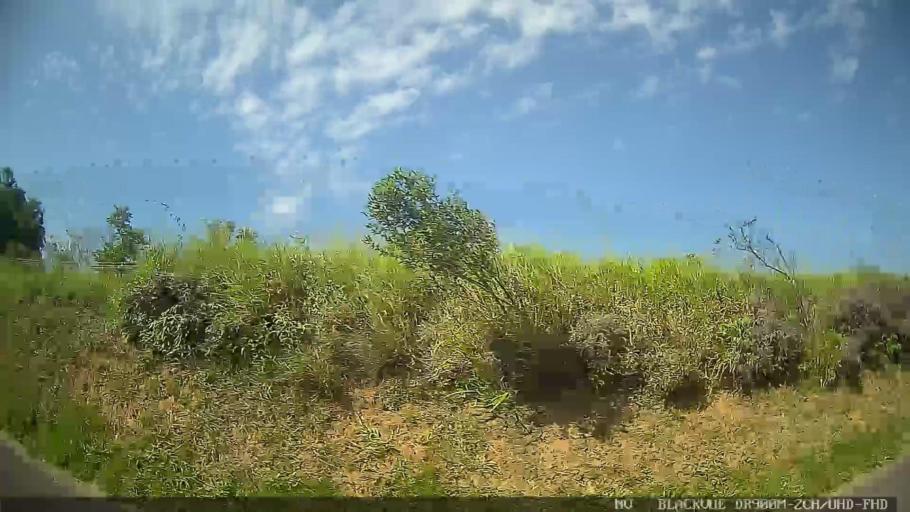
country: BR
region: Sao Paulo
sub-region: Jarinu
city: Jarinu
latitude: -23.0532
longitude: -46.6642
